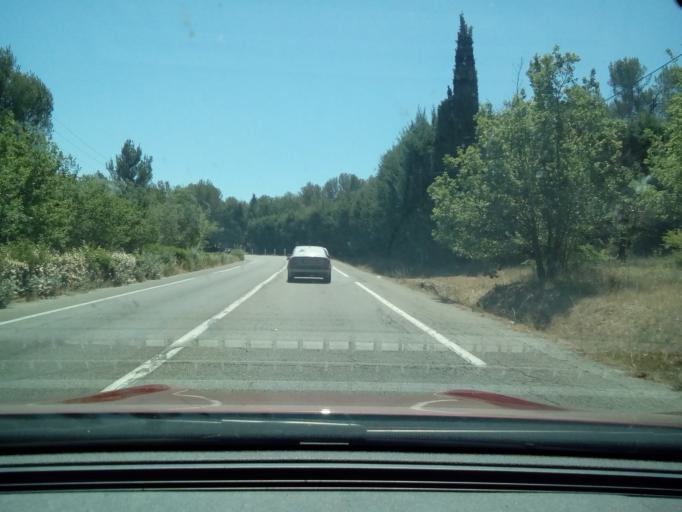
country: FR
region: Provence-Alpes-Cote d'Azur
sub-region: Departement des Bouches-du-Rhone
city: Rousset
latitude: 43.4617
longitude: 5.6218
